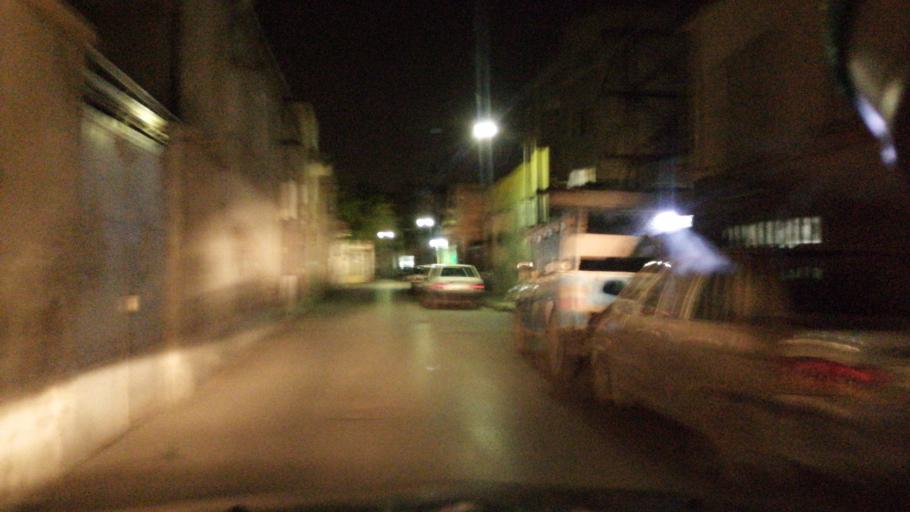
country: IR
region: Razavi Khorasan
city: Mashhad
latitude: 36.3078
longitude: 59.6044
